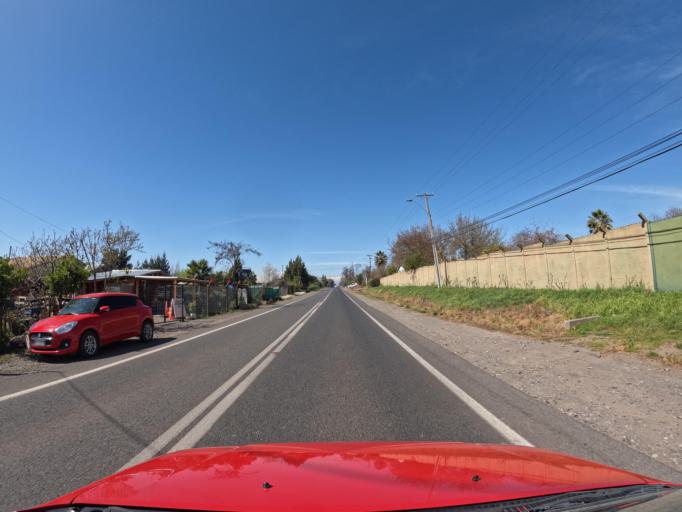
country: CL
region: Maule
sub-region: Provincia de Curico
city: Teno
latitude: -34.9633
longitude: -71.0709
